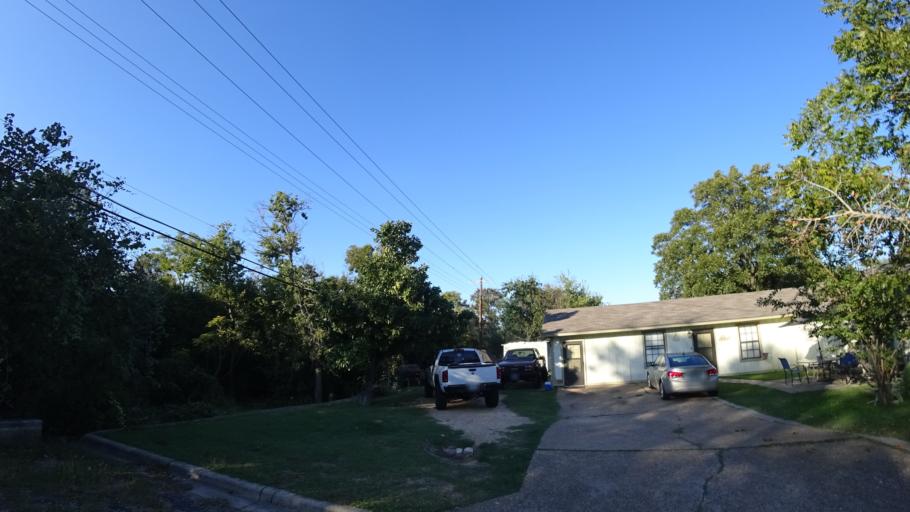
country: US
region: Texas
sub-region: Travis County
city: Austin
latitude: 30.2213
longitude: -97.7377
